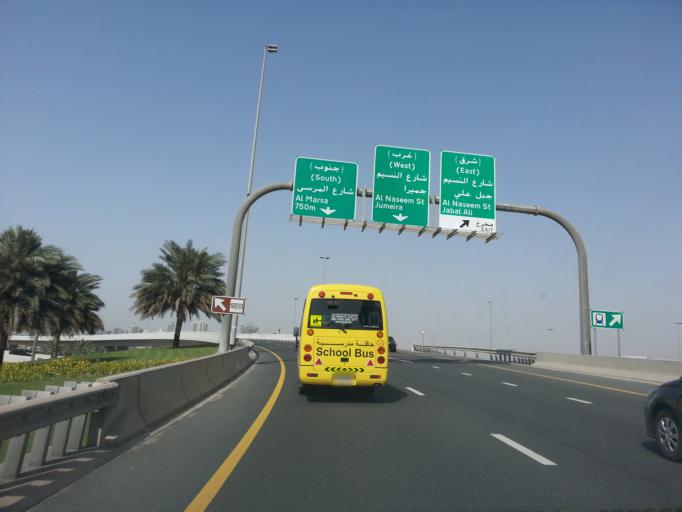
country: AE
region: Dubai
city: Dubai
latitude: 25.0816
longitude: 55.1527
